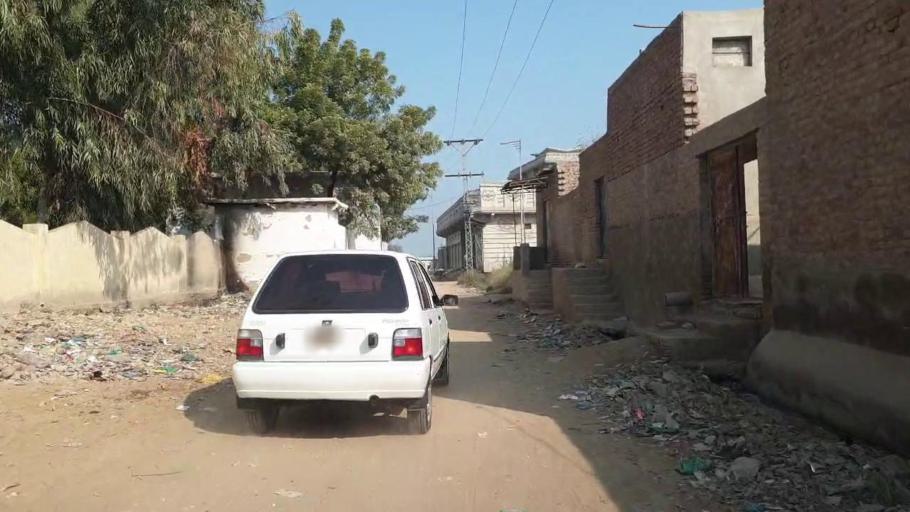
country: PK
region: Sindh
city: Bhit Shah
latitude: 25.7215
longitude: 68.5248
